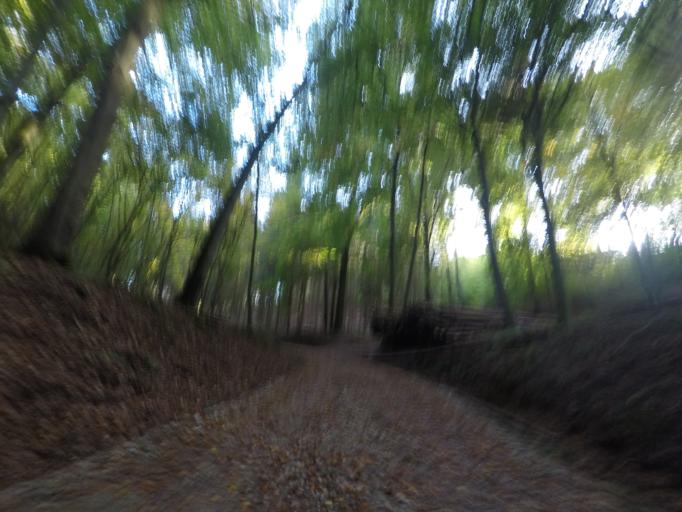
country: LU
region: Luxembourg
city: Itzig
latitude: 49.6000
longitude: 6.1642
